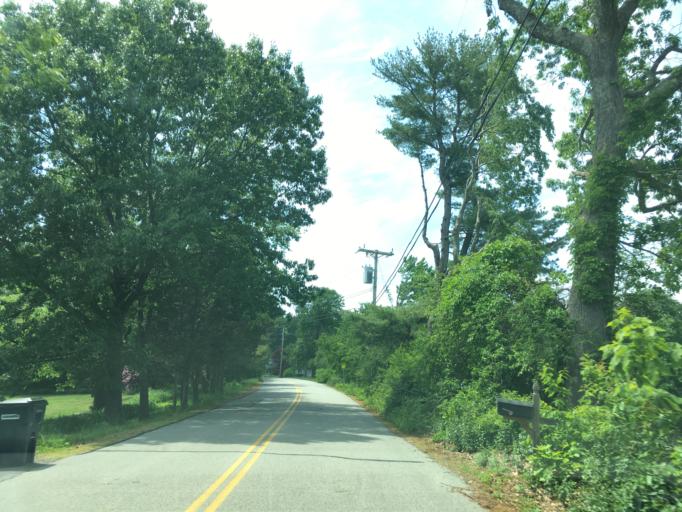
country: US
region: New Hampshire
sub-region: Rockingham County
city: Stratham Station
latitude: 43.0254
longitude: -70.8694
